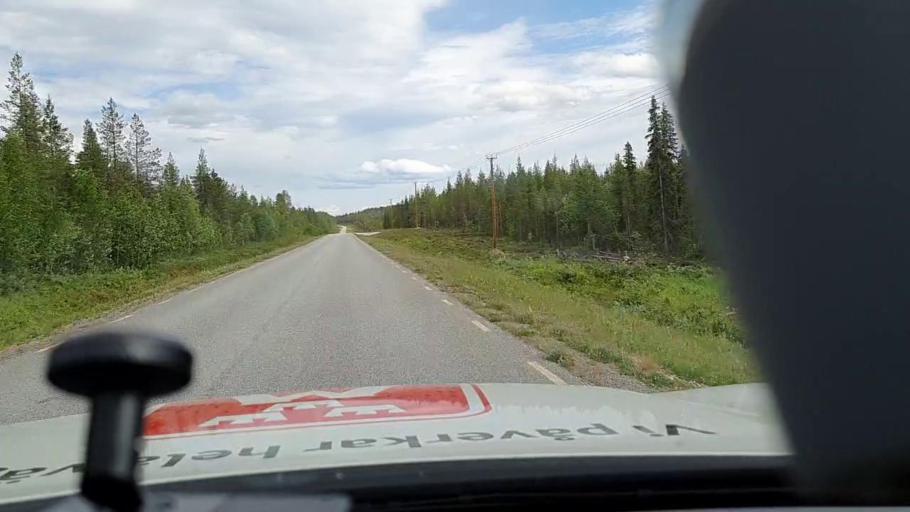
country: SE
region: Norrbotten
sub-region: Jokkmokks Kommun
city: Jokkmokk
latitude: 66.6567
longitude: 19.9739
